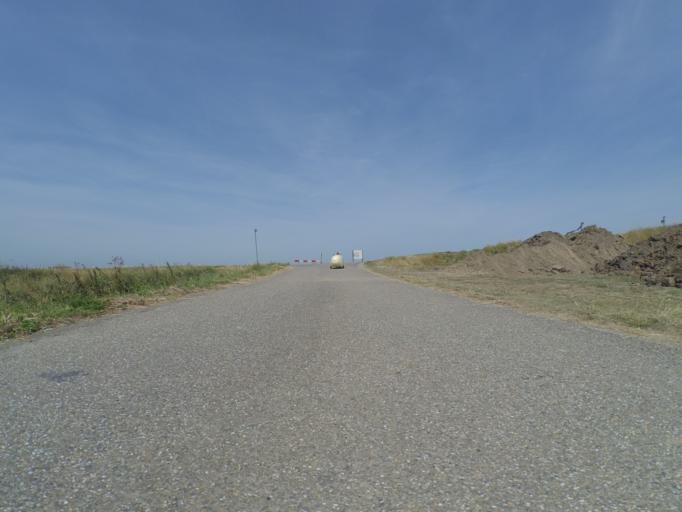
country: NL
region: North Brabant
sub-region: Gemeente Steenbergen
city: Nieuw-Vossemeer
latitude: 51.6363
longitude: 4.1807
